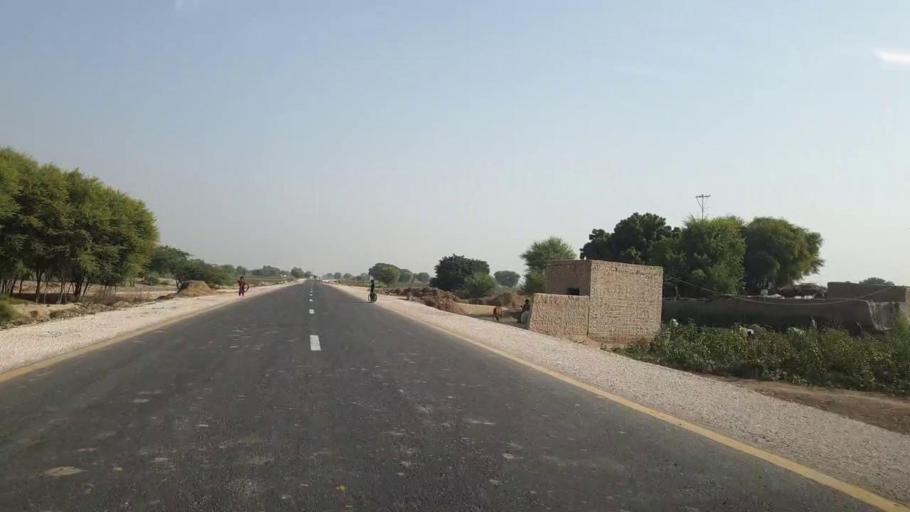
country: PK
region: Sindh
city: Sehwan
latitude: 26.4787
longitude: 67.7839
